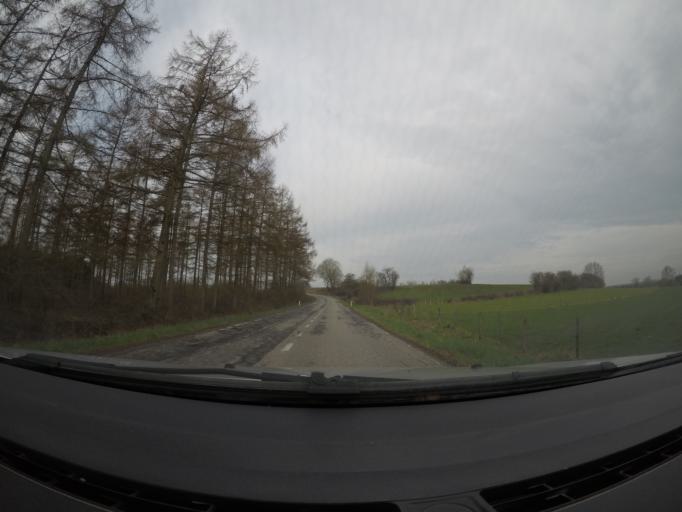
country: BE
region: Wallonia
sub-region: Province du Luxembourg
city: Tintigny
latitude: 49.7185
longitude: 5.5085
